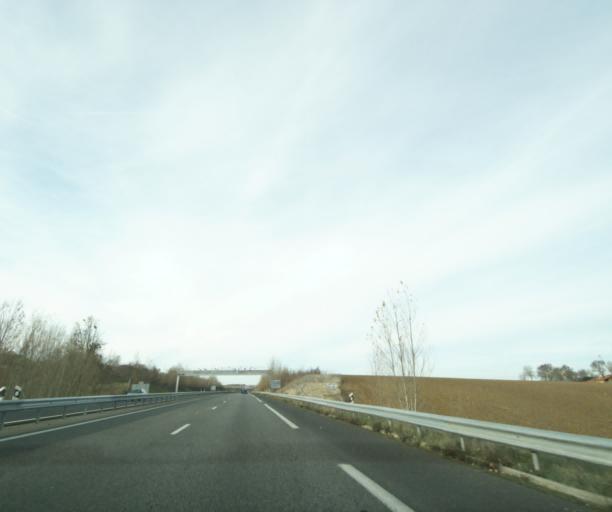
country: FR
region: Midi-Pyrenees
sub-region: Departement du Gers
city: Pujaudran
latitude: 43.6013
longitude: 1.0858
